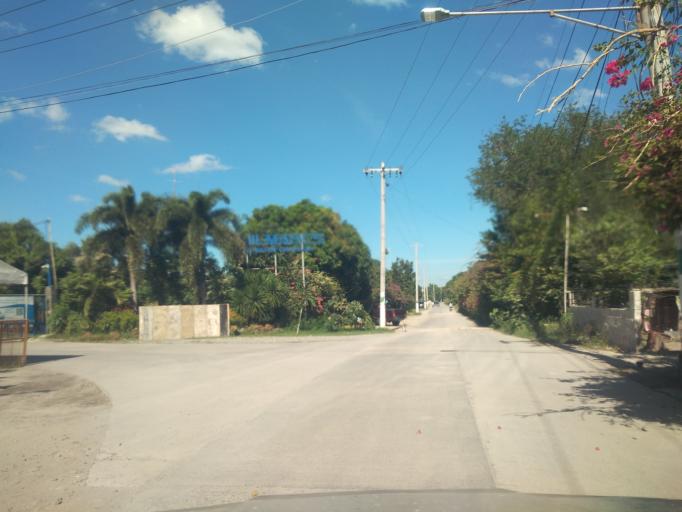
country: PH
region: Central Luzon
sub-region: Province of Pampanga
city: Bacolor
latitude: 15.0056
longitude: 120.6418
